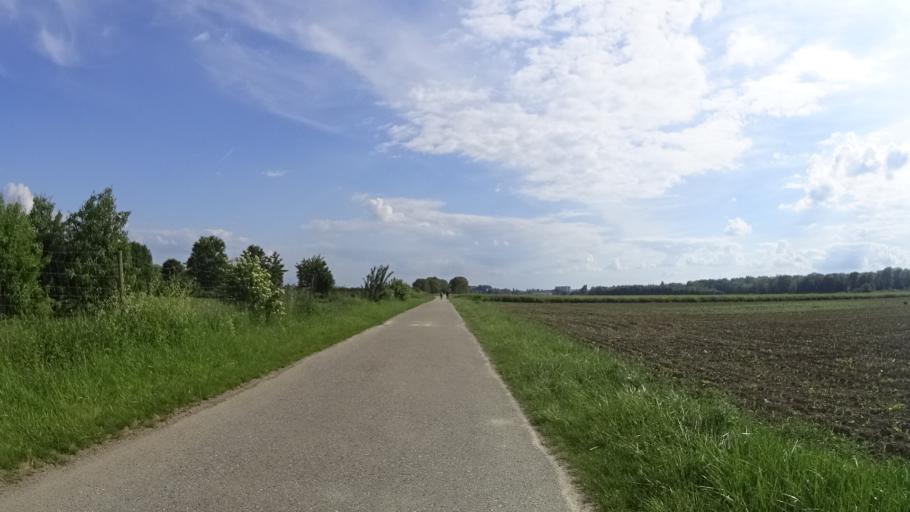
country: DE
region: Baden-Wuerttemberg
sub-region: Freiburg Region
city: Breisach am Rhein
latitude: 48.0598
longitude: 7.5884
